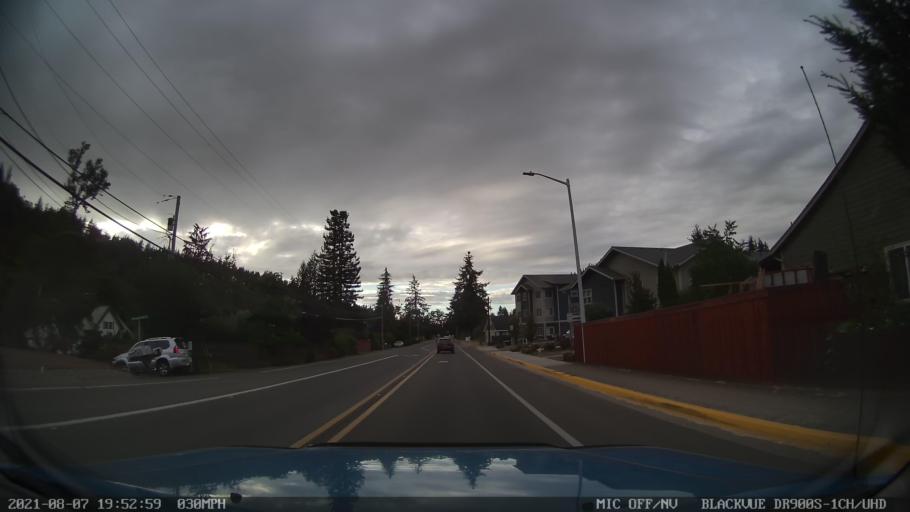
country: US
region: Oregon
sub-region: Marion County
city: Silverton
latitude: 44.9867
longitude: -122.7628
